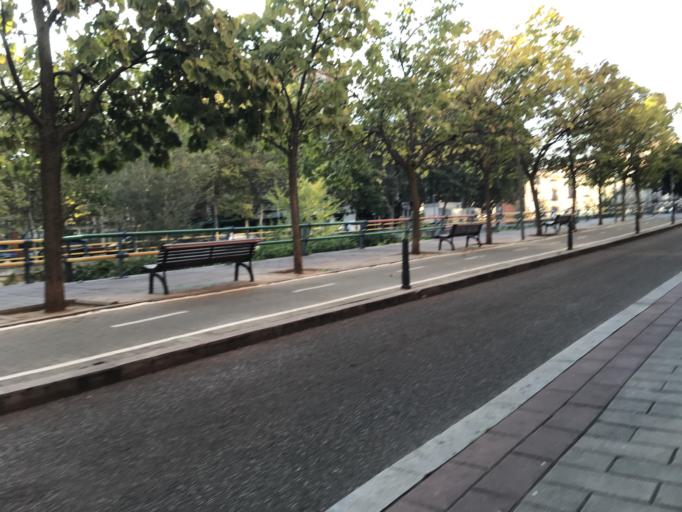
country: ES
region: Castille and Leon
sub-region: Provincia de Valladolid
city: Valladolid
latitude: 41.6531
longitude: -4.7120
